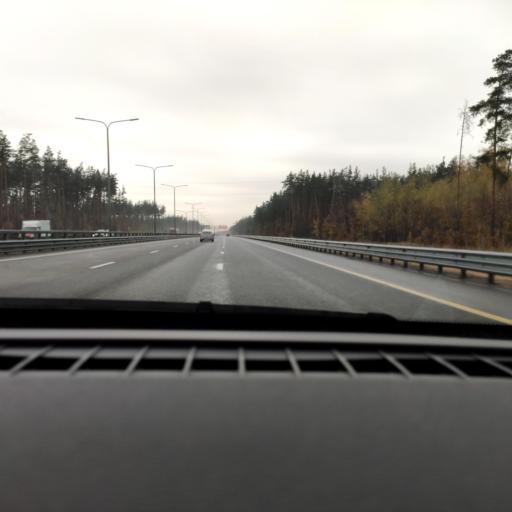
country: RU
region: Voronezj
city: Somovo
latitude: 51.7067
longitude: 39.3066
